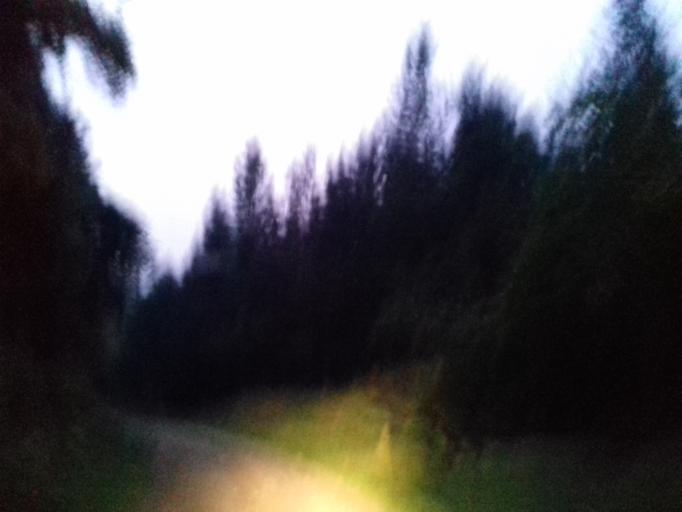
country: CO
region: Quindio
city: Salento
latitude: 4.5956
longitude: -75.5326
